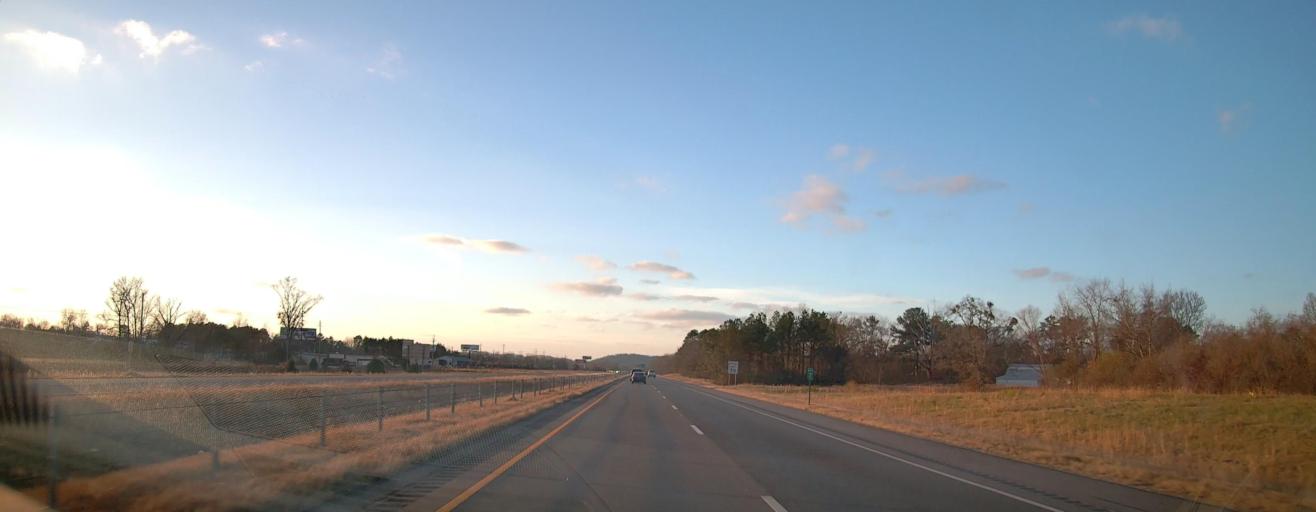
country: US
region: Alabama
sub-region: Etowah County
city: Rainbow City
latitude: 33.9948
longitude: -86.0485
